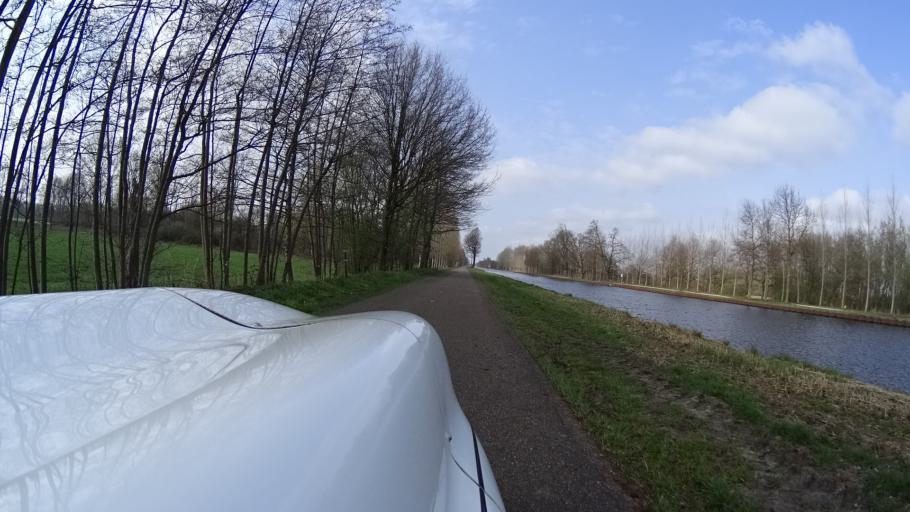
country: NL
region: North Brabant
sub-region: Gemeente Son en Breugel
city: Breugel
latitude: 51.5089
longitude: 5.5352
